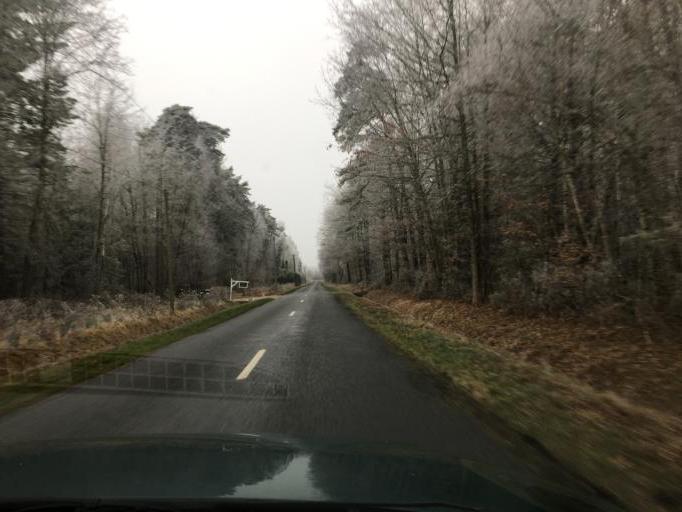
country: FR
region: Centre
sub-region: Departement du Loir-et-Cher
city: Chaumont-sur-Tharonne
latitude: 47.6696
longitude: 1.8877
